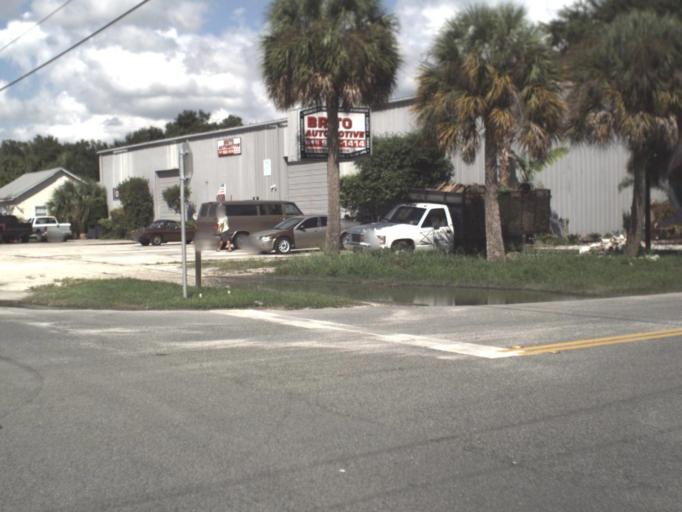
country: US
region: Florida
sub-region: Sarasota County
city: Osprey
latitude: 27.2021
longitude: -82.4902
